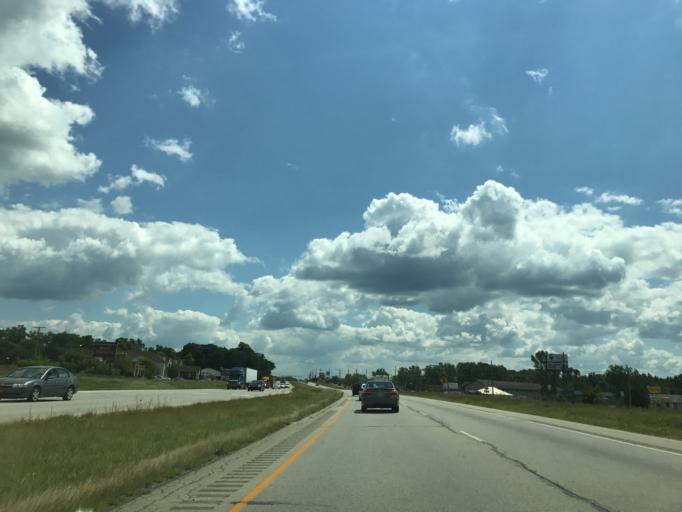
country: US
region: Indiana
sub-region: Kosciusko County
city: Winona Lake
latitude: 41.2384
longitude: -85.8151
